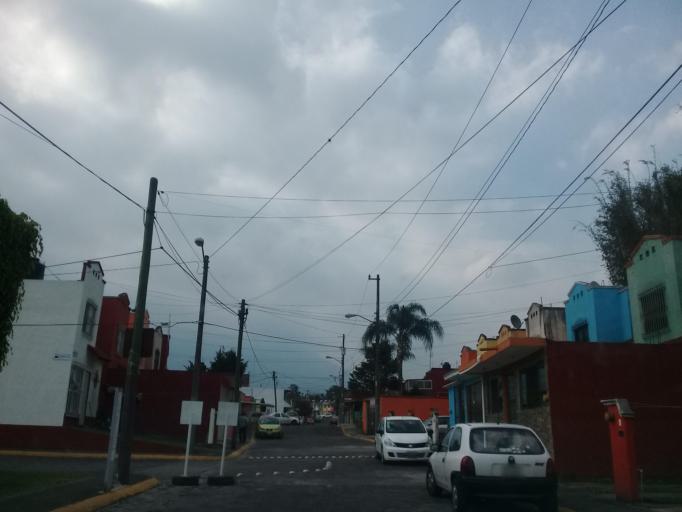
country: MX
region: Veracruz
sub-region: Mariano Escobedo
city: Palmira
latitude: 18.8734
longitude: -97.1073
